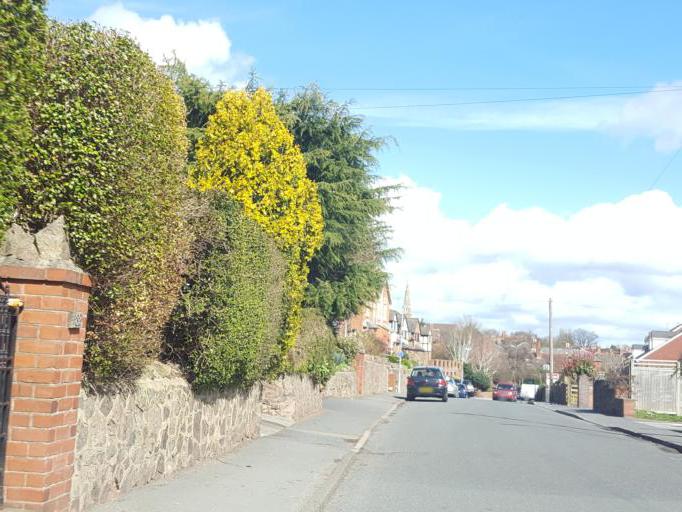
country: GB
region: England
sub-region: Worcestershire
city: Great Malvern
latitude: 52.1049
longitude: -2.3187
